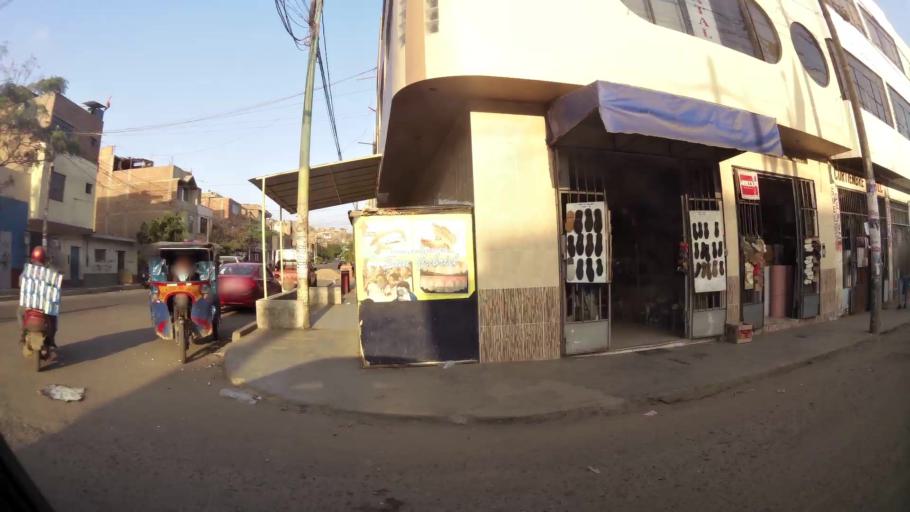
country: PE
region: La Libertad
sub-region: Provincia de Trujillo
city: El Porvenir
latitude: -8.0824
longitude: -79.0008
